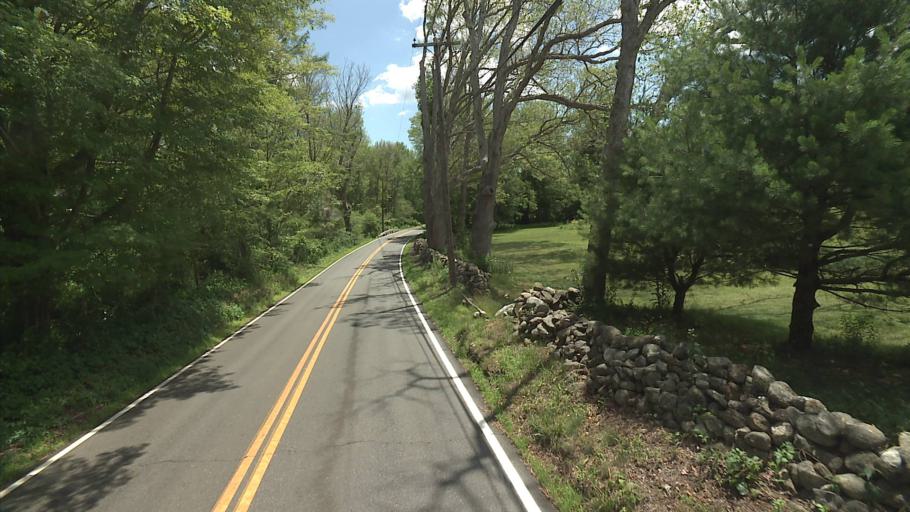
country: US
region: Connecticut
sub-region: New London County
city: Colchester
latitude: 41.4919
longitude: -72.3460
